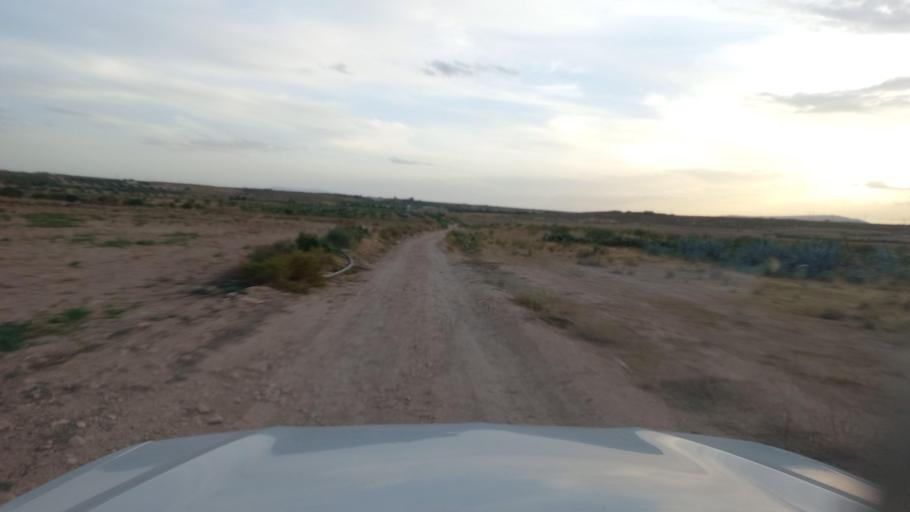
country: TN
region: Al Qasrayn
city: Sbiba
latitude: 35.4157
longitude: 9.0862
